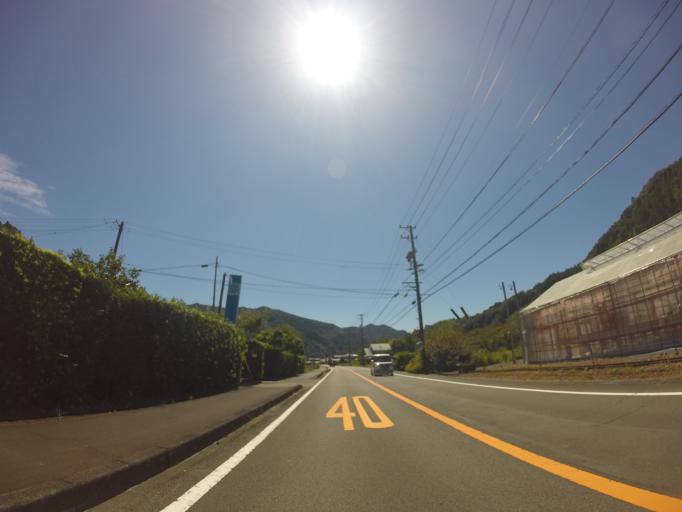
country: JP
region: Shizuoka
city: Fujieda
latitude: 34.9254
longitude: 138.2053
